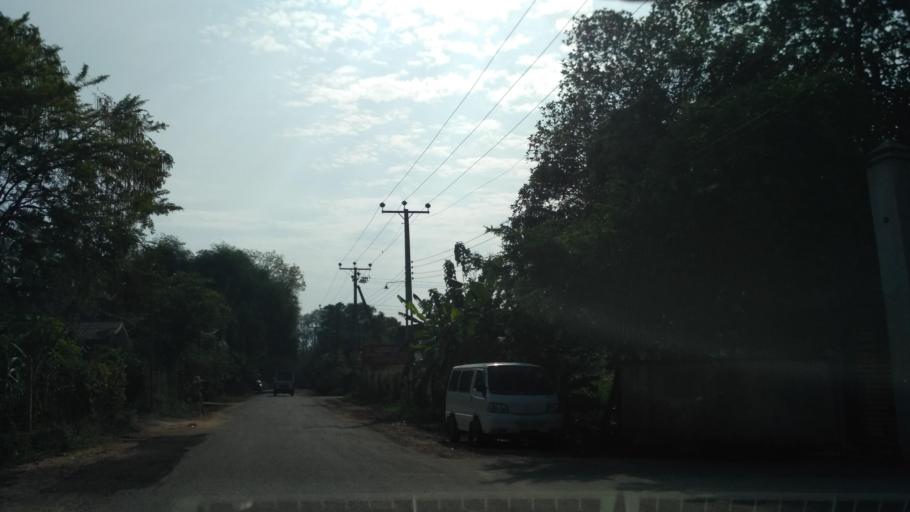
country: LK
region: North Western
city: Kuliyapitiya
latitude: 7.3265
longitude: 80.0215
